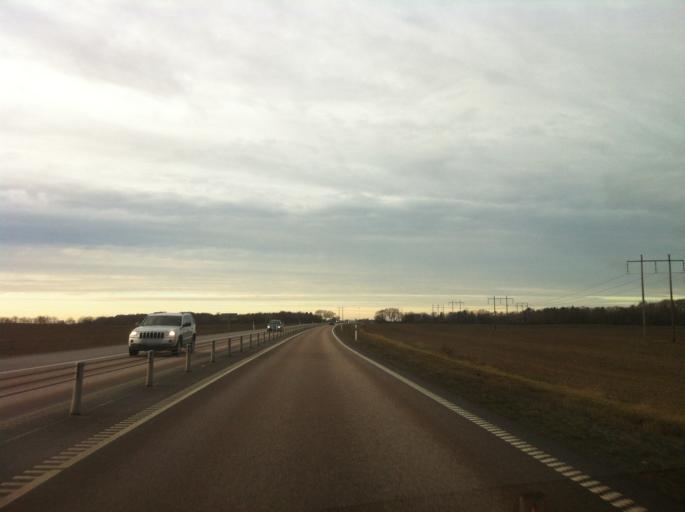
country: SE
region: Skane
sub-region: Helsingborg
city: Odakra
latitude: 56.0934
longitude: 12.6939
